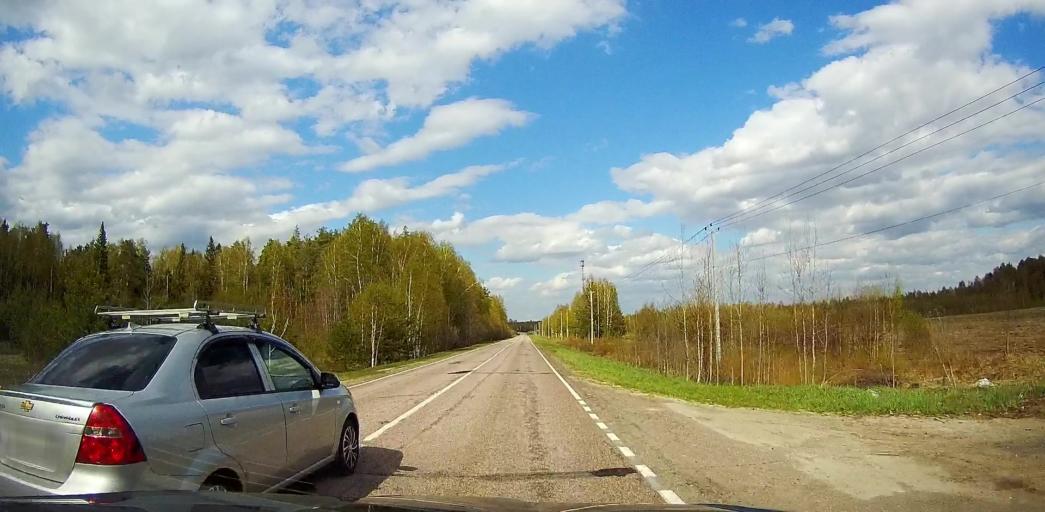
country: RU
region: Moskovskaya
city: Rakhmanovo
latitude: 55.6643
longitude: 38.6413
